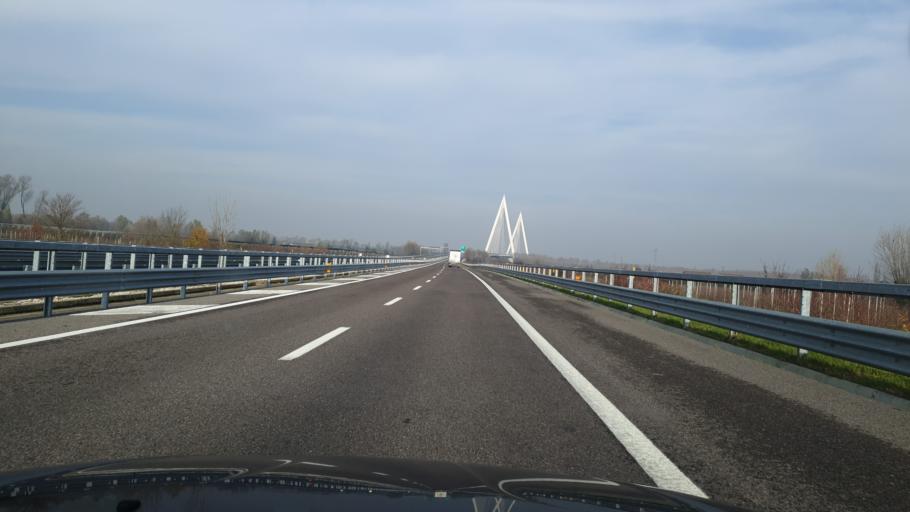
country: IT
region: Veneto
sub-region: Provincia di Padova
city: Piacenza d'Adige
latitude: 45.1099
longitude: 11.5298
